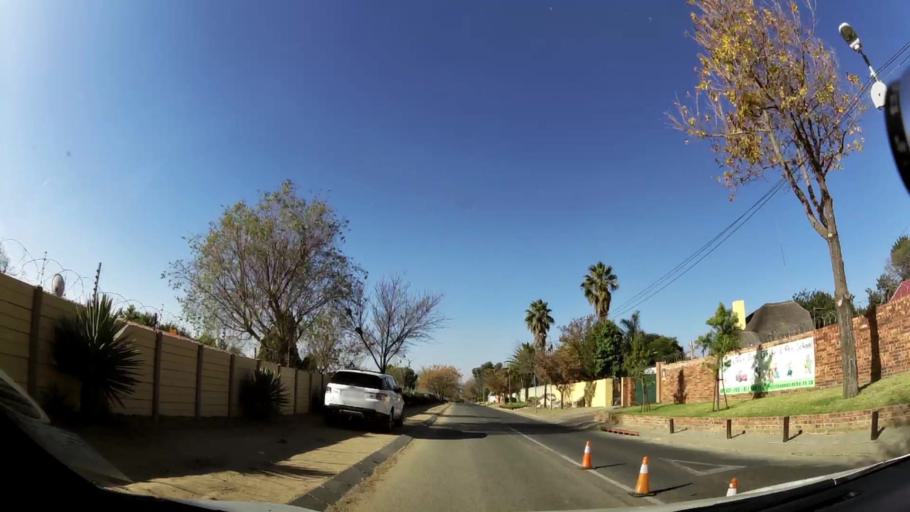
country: ZA
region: Gauteng
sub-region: City of Johannesburg Metropolitan Municipality
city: Diepsloot
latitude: -26.0234
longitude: 27.9673
